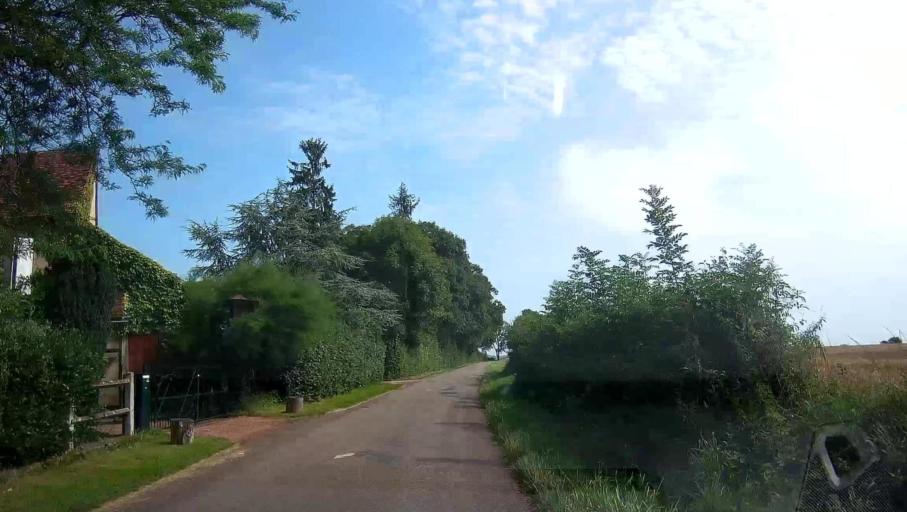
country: FR
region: Bourgogne
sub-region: Departement de Saone-et-Loire
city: Saint-Leger-sur-Dheune
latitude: 46.8977
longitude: 4.6238
